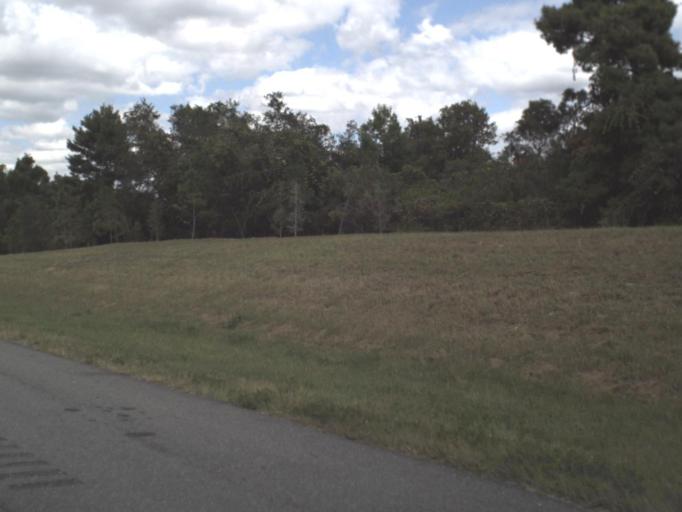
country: US
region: Florida
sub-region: Orange County
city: Orlovista
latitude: 28.5002
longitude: -81.4796
